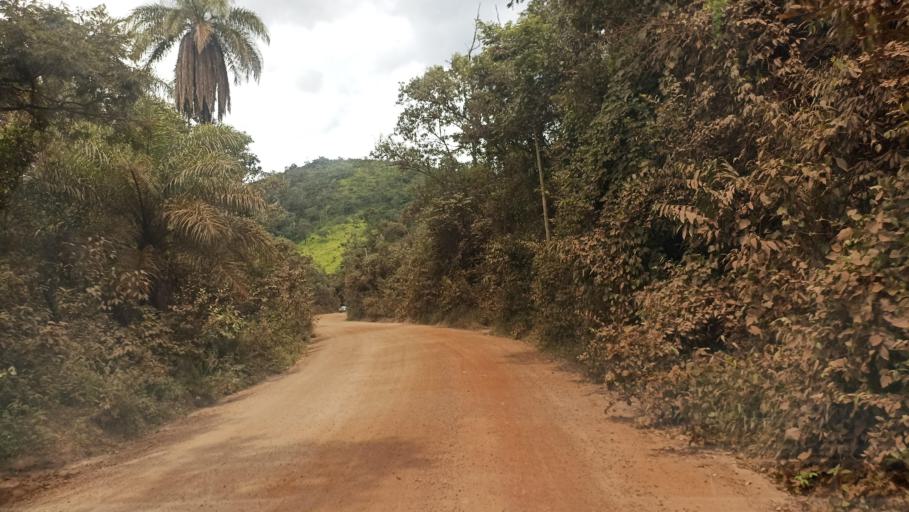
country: BR
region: Minas Gerais
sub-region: Itabirito
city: Itabirito
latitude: -20.3655
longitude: -43.7624
